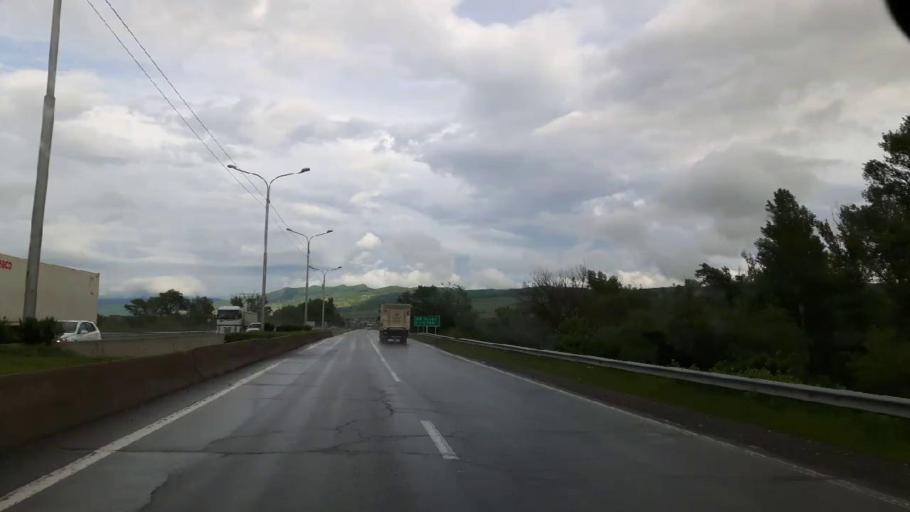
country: GE
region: Shida Kartli
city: Kaspi
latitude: 41.9093
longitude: 44.5697
